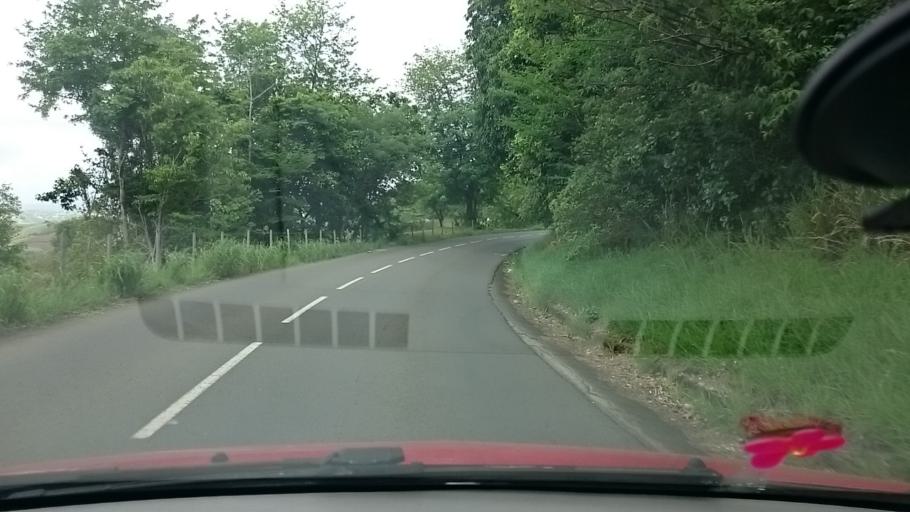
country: MQ
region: Martinique
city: Petite Riviere Salee
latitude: 14.7565
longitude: -60.9273
